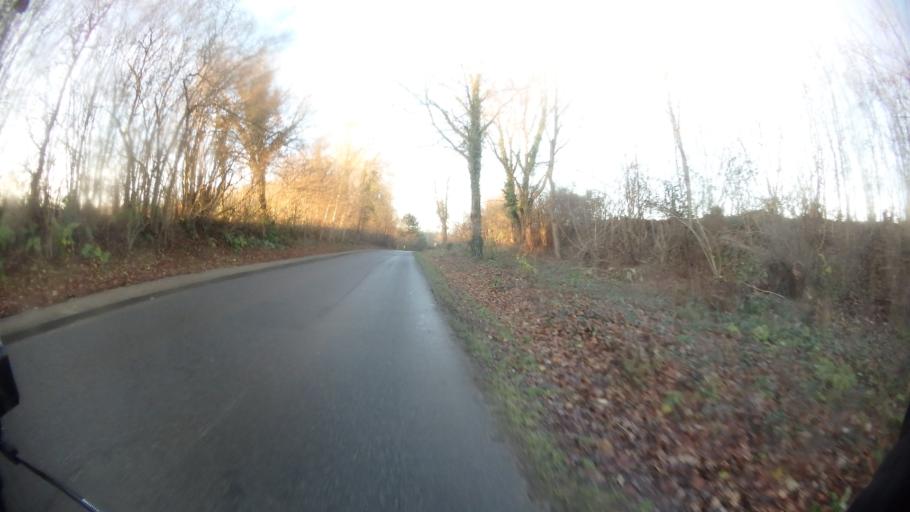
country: DE
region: Schleswig-Holstein
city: Susel
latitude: 54.0179
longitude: 10.7012
